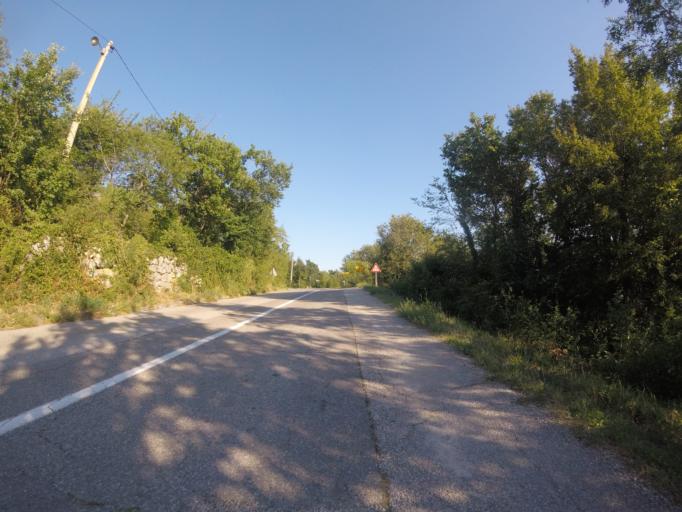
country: HR
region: Primorsko-Goranska
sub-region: Grad Crikvenica
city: Crikvenica
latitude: 45.2154
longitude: 14.7004
